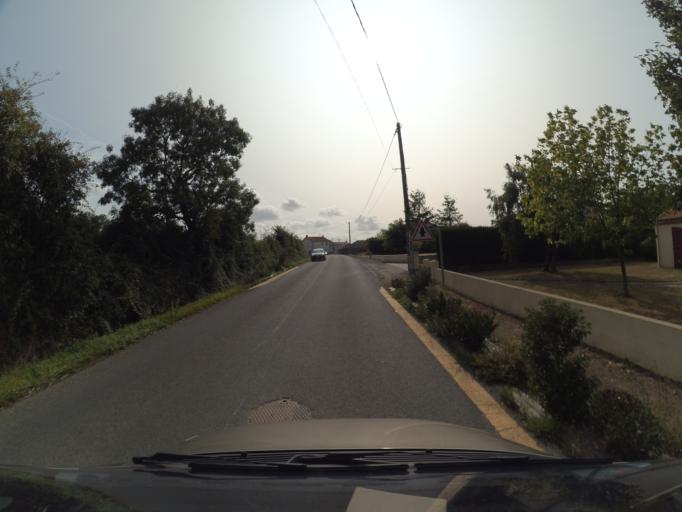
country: FR
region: Pays de la Loire
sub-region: Departement de la Vendee
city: Treize-Septiers
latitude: 46.9794
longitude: -1.2399
